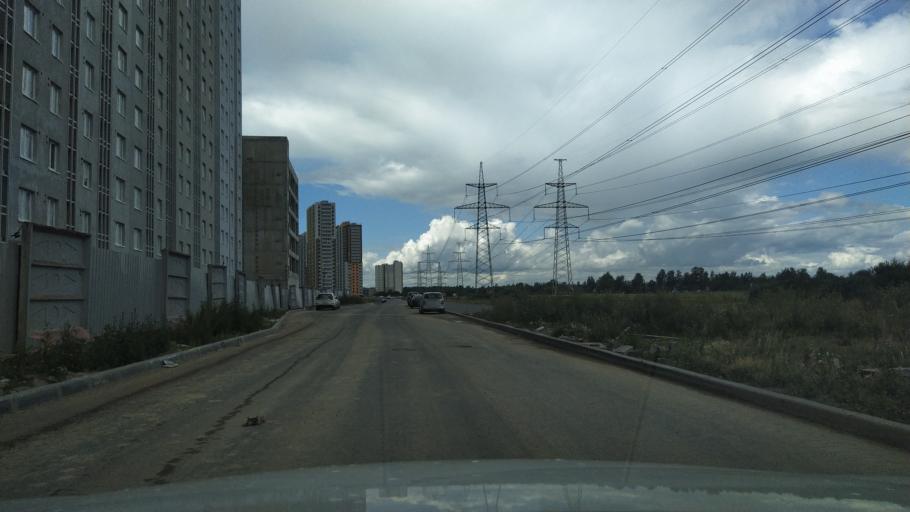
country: RU
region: St.-Petersburg
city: Krasnogvargeisky
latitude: 60.0025
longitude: 30.4831
